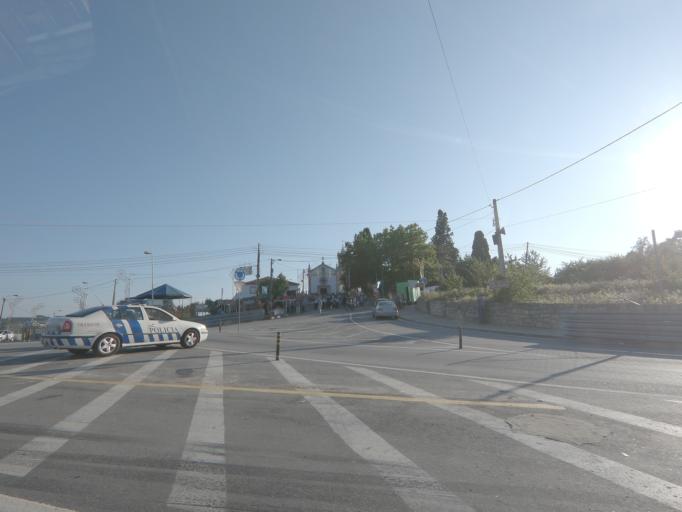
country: PT
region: Vila Real
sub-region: Vila Real
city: Vila Real
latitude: 41.3002
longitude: -7.7159
